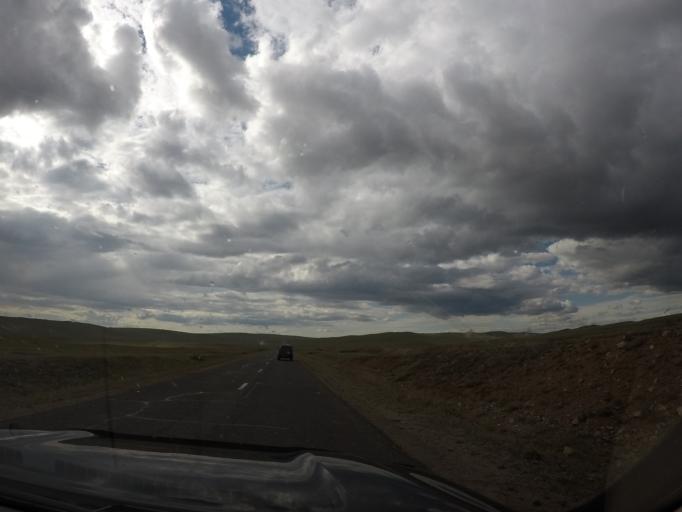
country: MN
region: Hentiy
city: Modot
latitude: 47.5563
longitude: 109.3462
